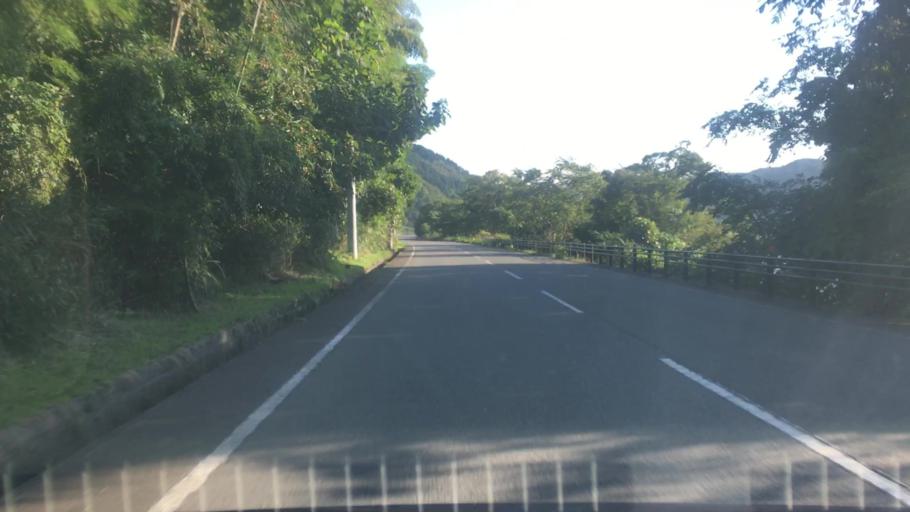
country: JP
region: Hyogo
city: Toyooka
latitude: 35.6030
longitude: 134.8059
